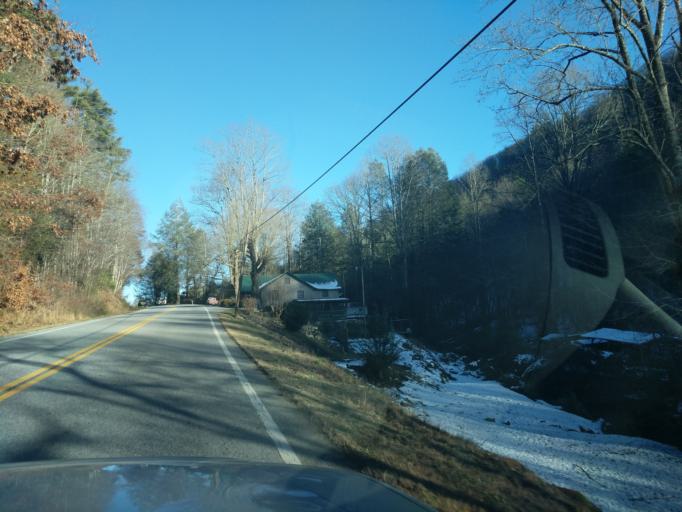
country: US
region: Georgia
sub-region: Rabun County
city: Clayton
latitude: 34.8608
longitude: -83.5019
